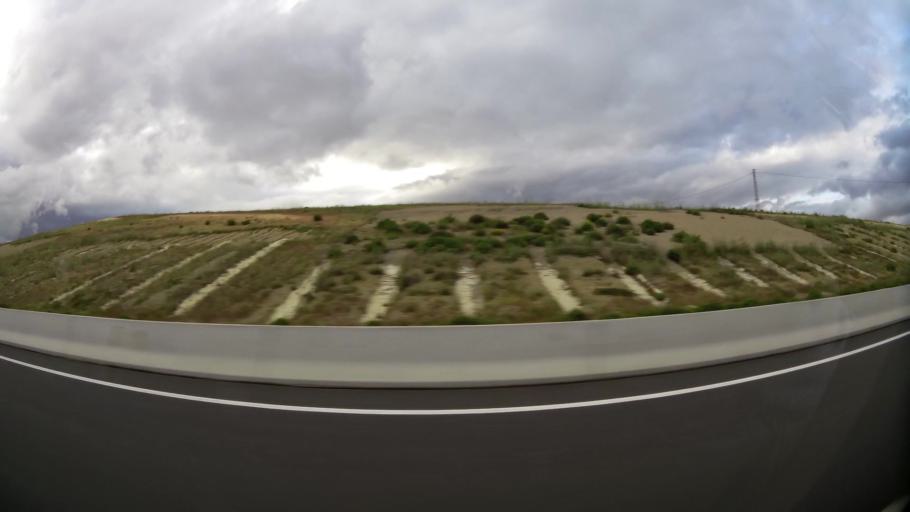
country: MA
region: Taza-Al Hoceima-Taounate
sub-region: Taza
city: Taza
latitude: 34.2515
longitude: -3.8998
